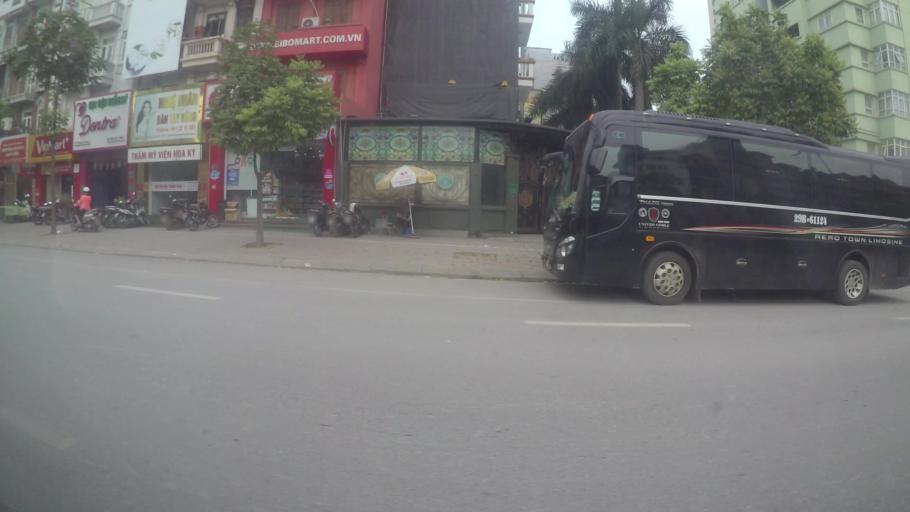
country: VN
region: Ha Noi
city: Cau Dien
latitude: 21.0312
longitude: 105.7745
